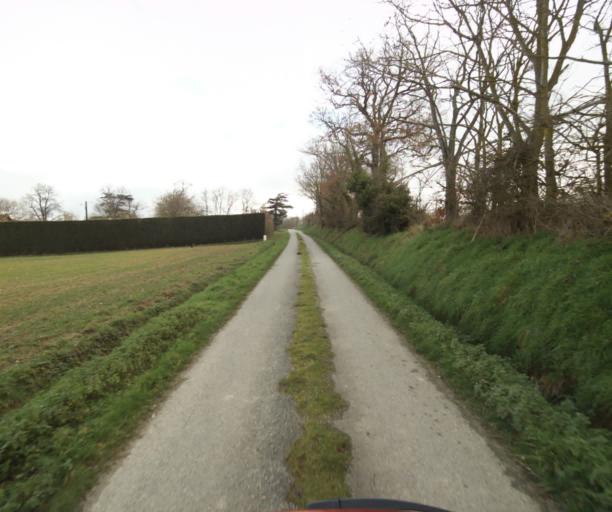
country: FR
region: Midi-Pyrenees
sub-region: Departement de l'Ariege
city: Mazeres
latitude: 43.2302
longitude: 1.7122
